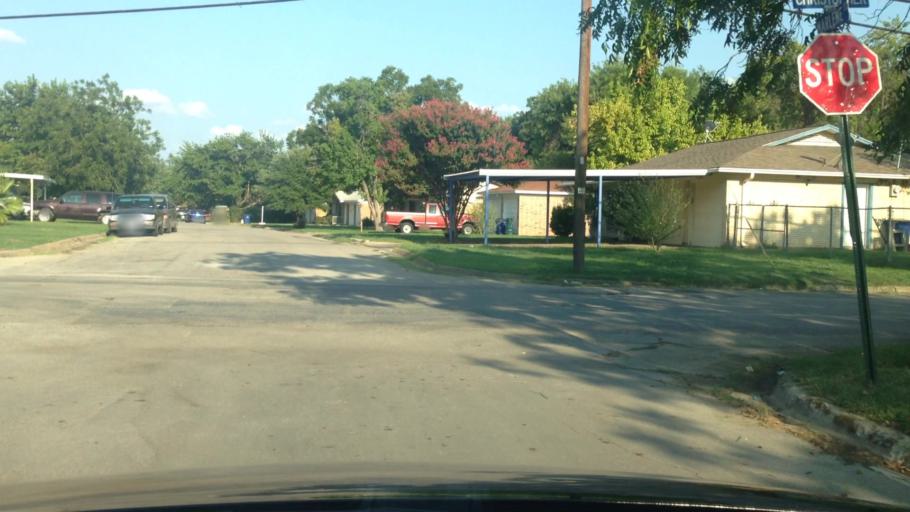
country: US
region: Texas
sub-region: Tarrant County
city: Everman
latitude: 32.6283
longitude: -97.2951
